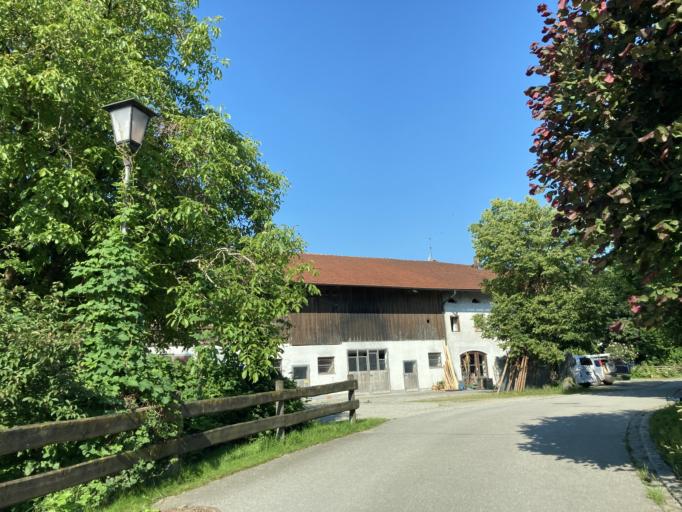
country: DE
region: Bavaria
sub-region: Upper Bavaria
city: Bad Endorf
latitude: 47.8992
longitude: 12.2794
